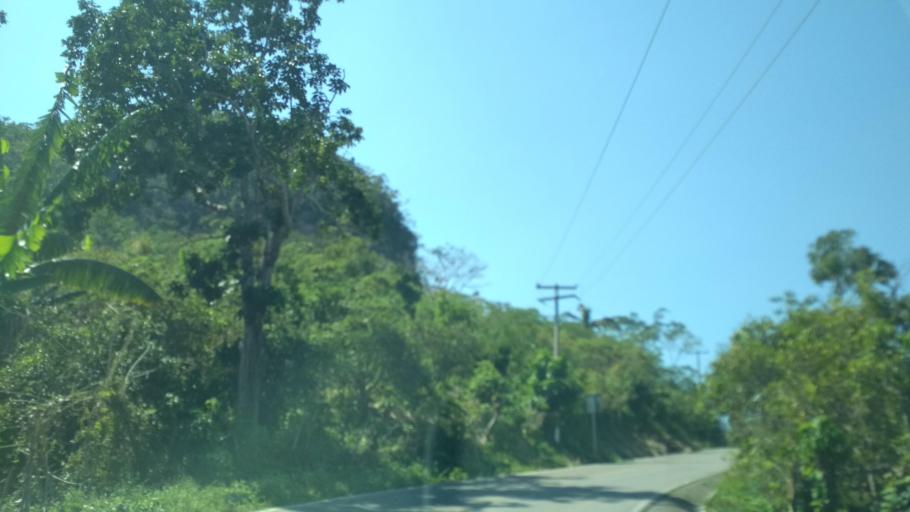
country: MX
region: Veracruz
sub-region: Papantla
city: Polutla
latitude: 20.4742
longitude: -97.2138
